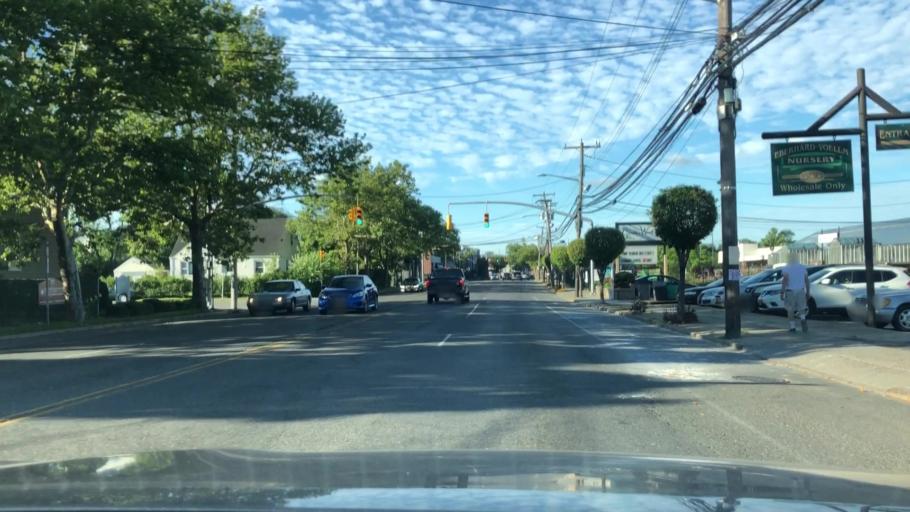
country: US
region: New York
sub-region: Nassau County
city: Franklin Square
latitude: 40.6967
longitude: -73.6826
